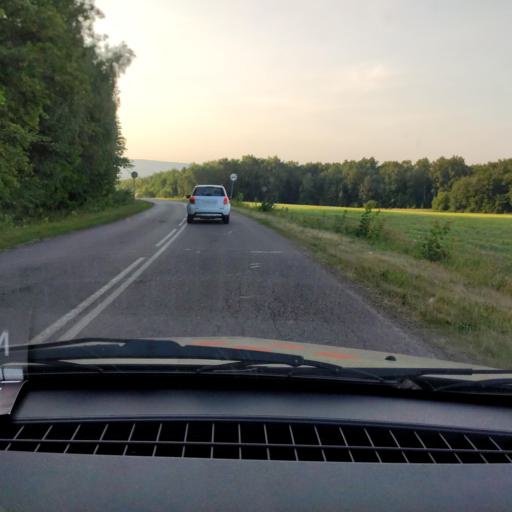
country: RU
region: Bashkortostan
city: Avdon
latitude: 54.5706
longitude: 55.6762
